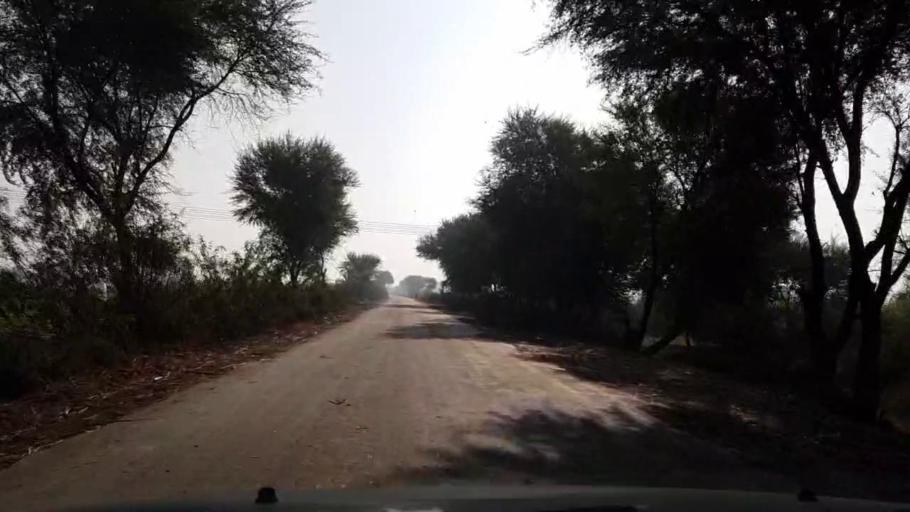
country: PK
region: Sindh
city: Matiari
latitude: 25.5751
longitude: 68.5061
